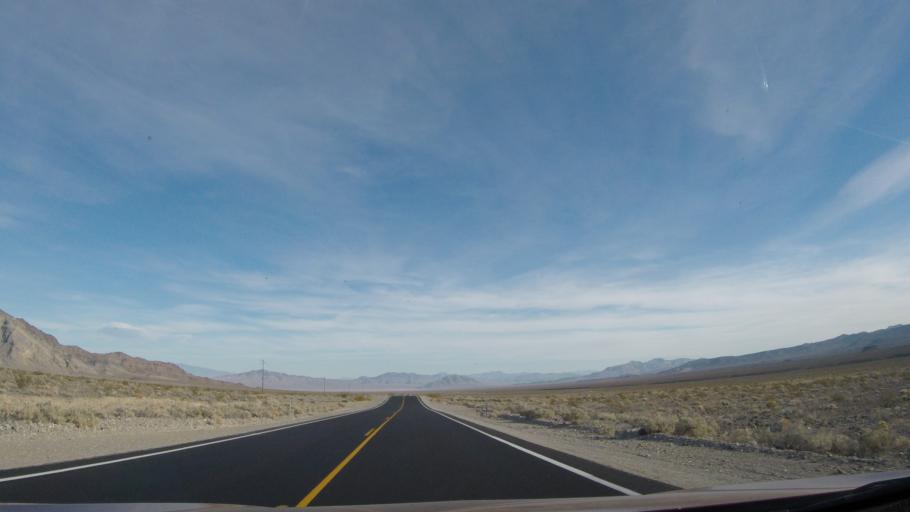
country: US
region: Nevada
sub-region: Nye County
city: Pahrump
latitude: 36.3239
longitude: -116.5607
